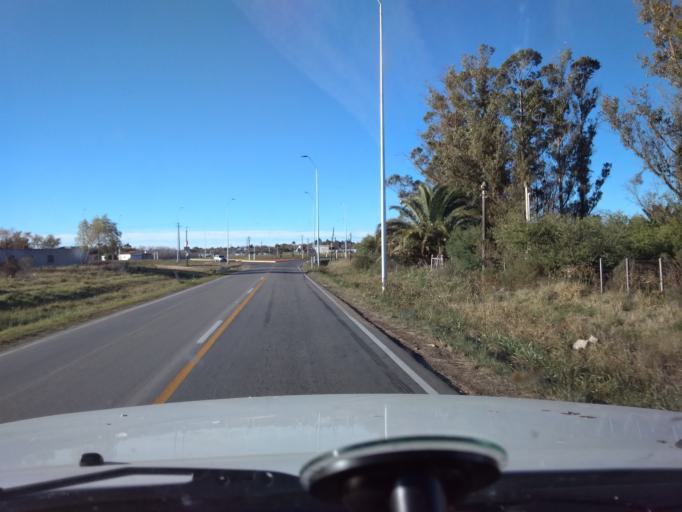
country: UY
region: Canelones
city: Santa Rosa
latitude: -34.5062
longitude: -56.0501
